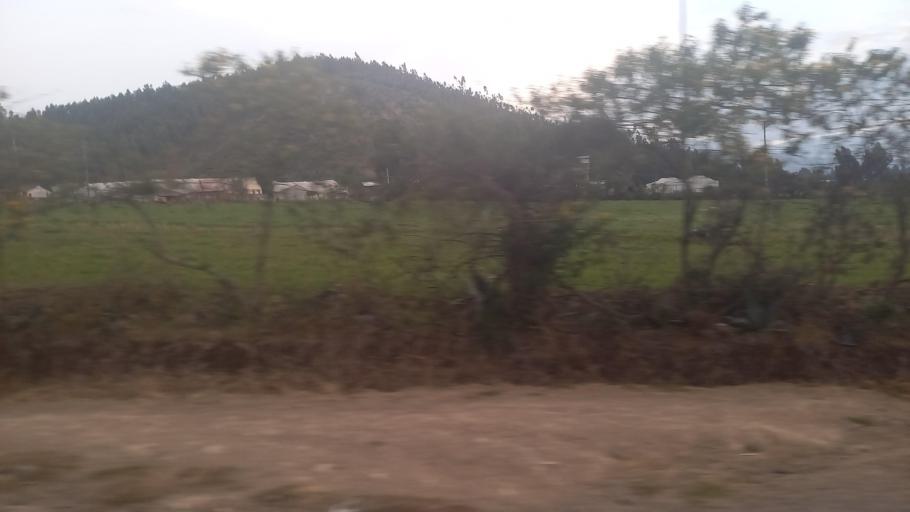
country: EC
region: Pichincha
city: Cayambe
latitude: 0.0704
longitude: -78.1151
